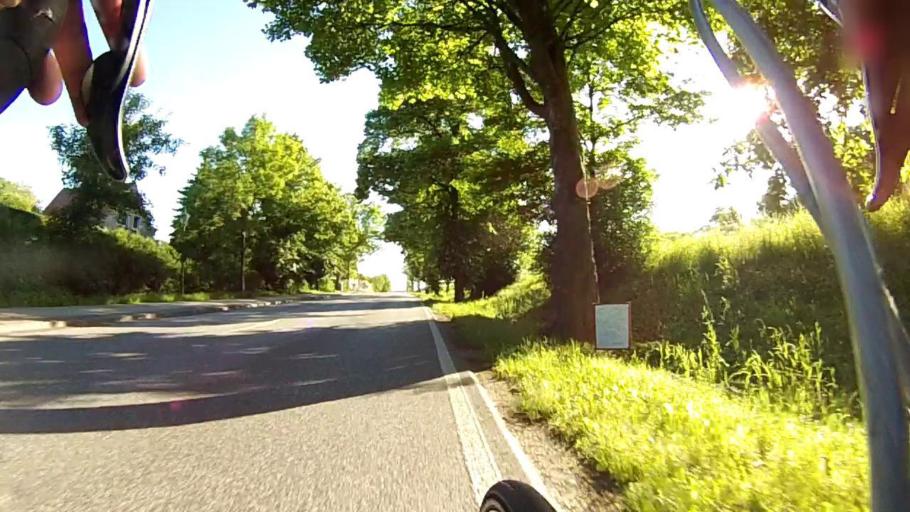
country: DE
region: Brandenburg
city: Ahrensfelde
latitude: 52.6053
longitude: 13.6143
